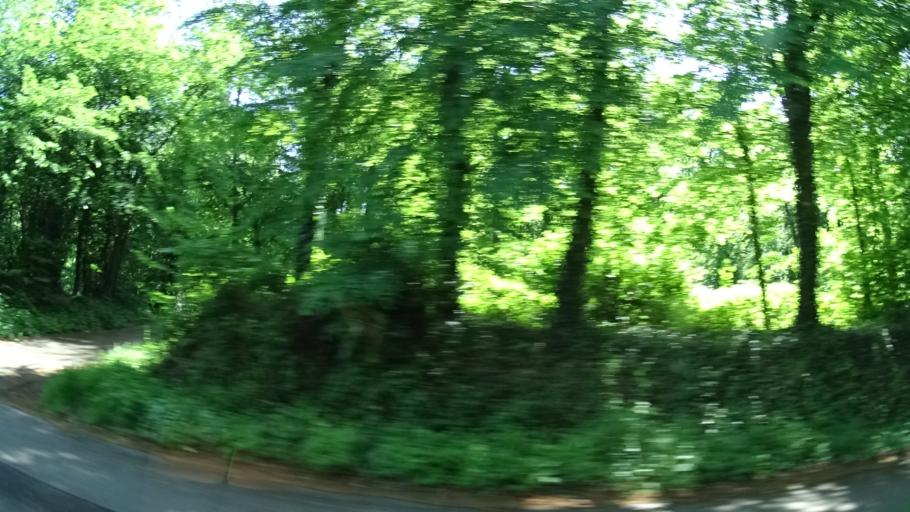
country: DE
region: Baden-Wuerttemberg
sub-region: Karlsruhe Region
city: Malsch
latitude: 48.9068
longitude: 8.3681
